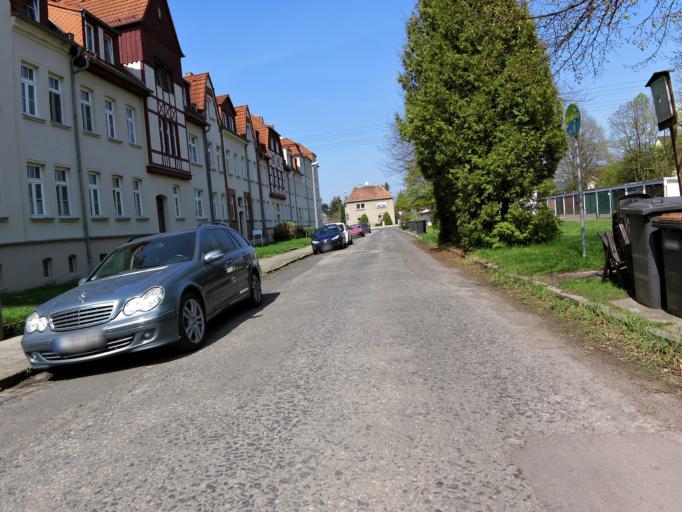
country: DE
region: Saxony
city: Leipzig
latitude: 51.3903
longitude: 12.3215
